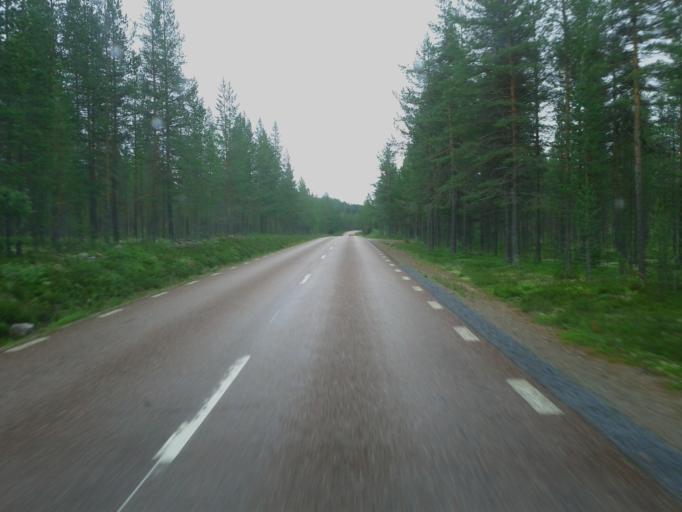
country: NO
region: Hedmark
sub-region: Trysil
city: Innbygda
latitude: 61.8031
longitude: 12.9121
